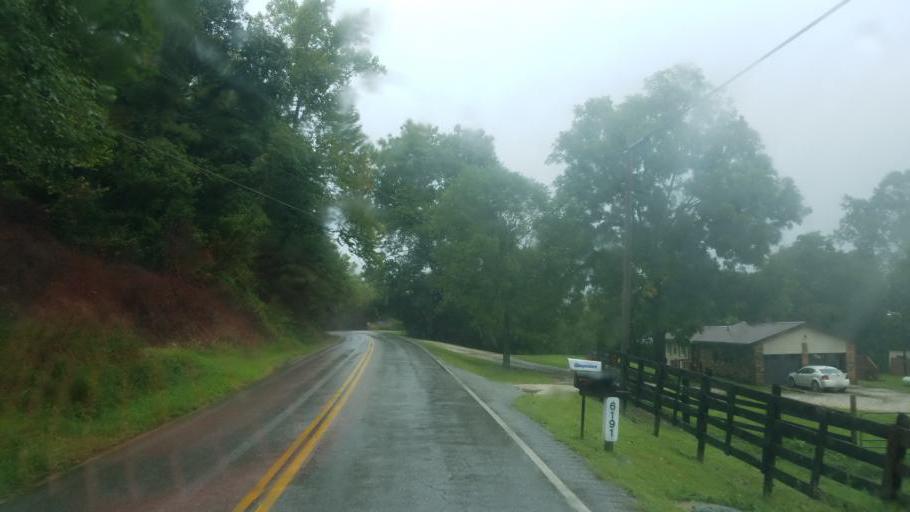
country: US
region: Ohio
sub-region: Scioto County
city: Franklin Furnace
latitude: 38.6605
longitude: -82.9185
